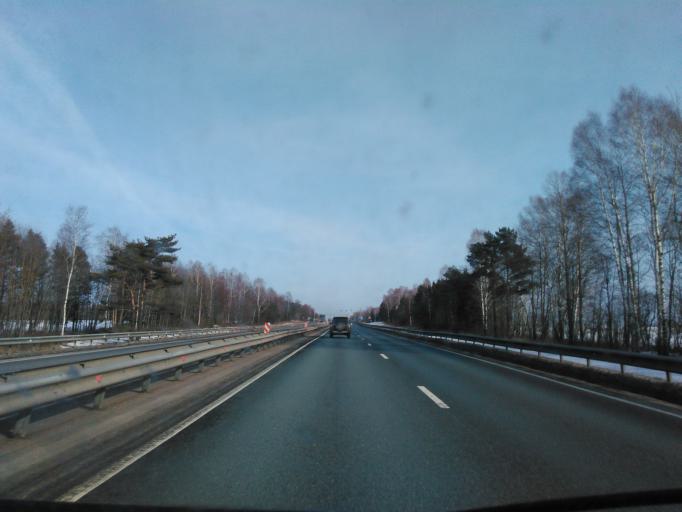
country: RU
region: Smolensk
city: Verkhnedneprovskiy
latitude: 55.1822
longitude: 33.5399
